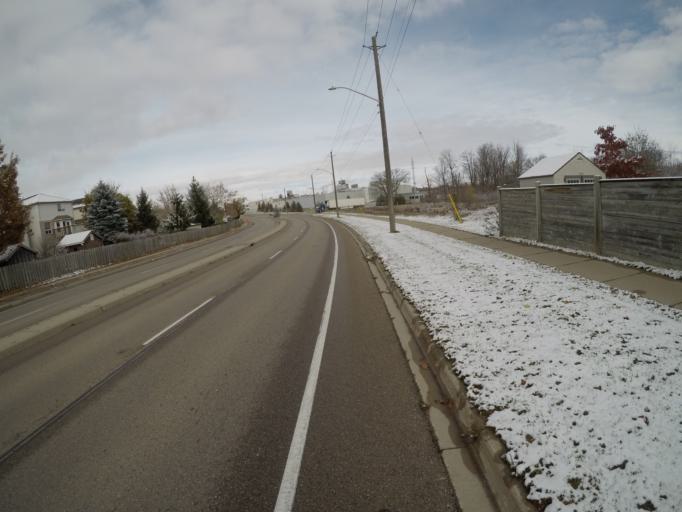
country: CA
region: Ontario
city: Waterloo
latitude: 43.4939
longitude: -80.4898
